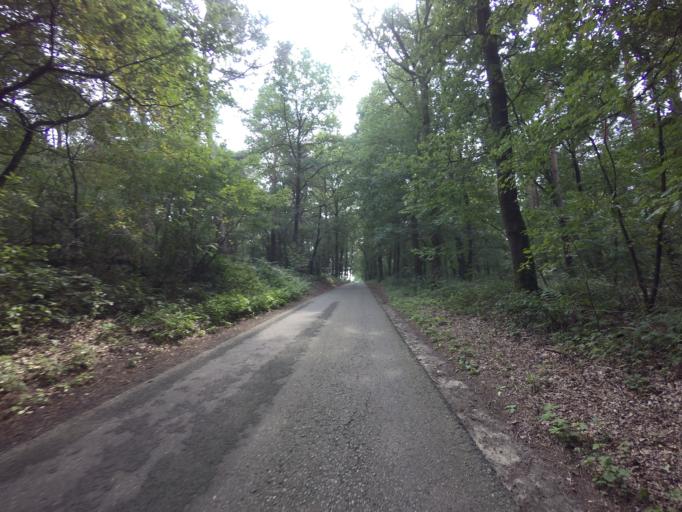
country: NL
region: Gelderland
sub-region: Gemeente Montferland
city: s-Heerenberg
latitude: 51.8815
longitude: 6.1784
